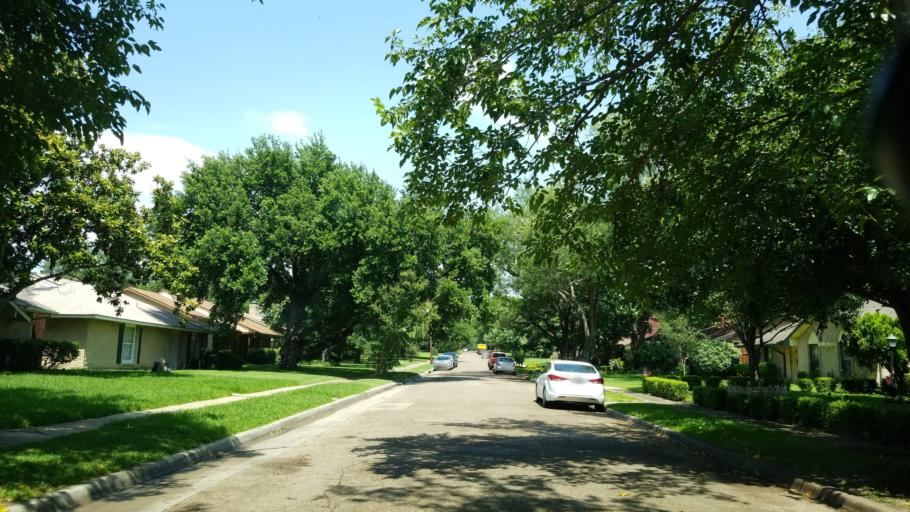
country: US
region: Texas
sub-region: Dallas County
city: Farmers Branch
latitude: 32.8782
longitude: -96.8748
